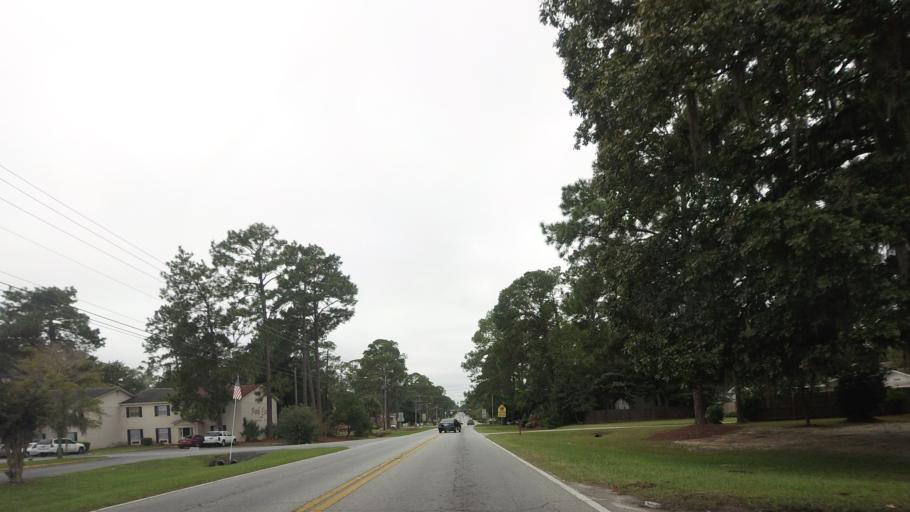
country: US
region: Georgia
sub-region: Lowndes County
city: Valdosta
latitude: 30.8575
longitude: -83.2640
